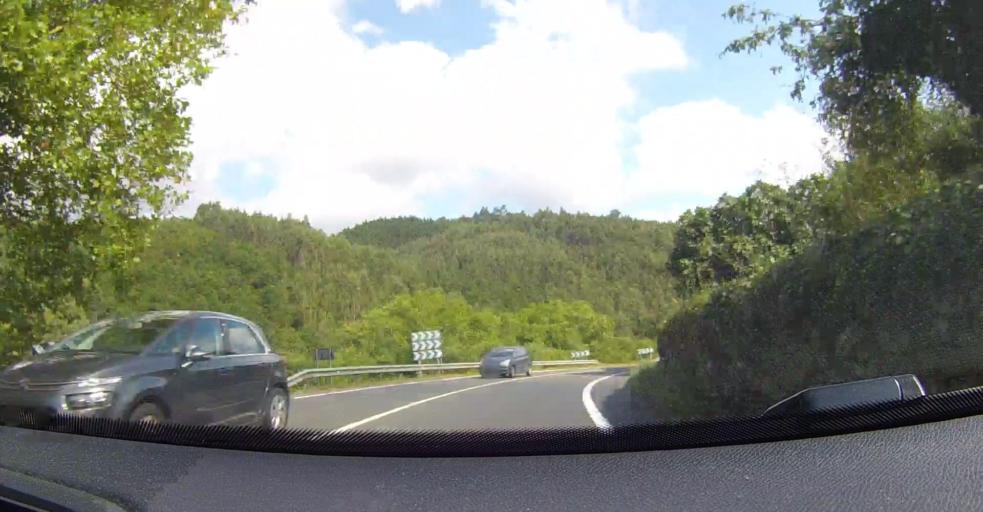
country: ES
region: Basque Country
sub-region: Bizkaia
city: Muxika
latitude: 43.2819
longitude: -2.6854
